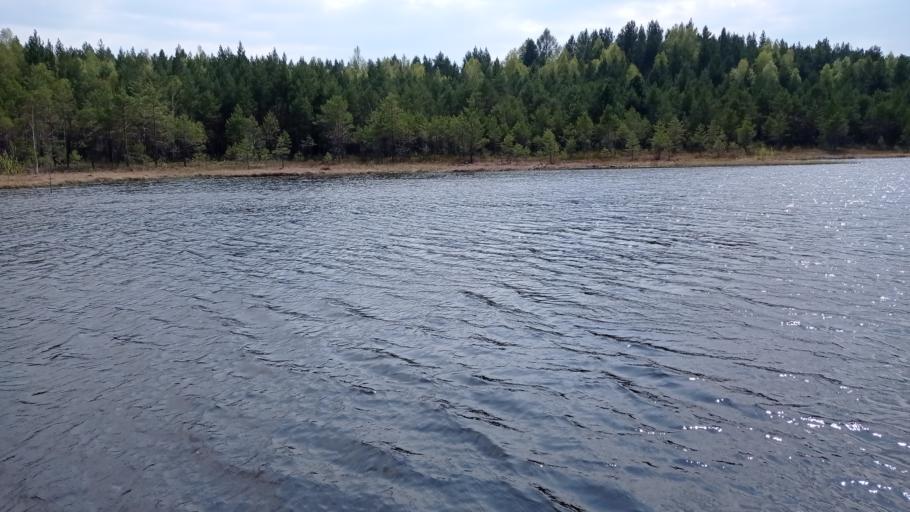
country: RU
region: Tomsk
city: Timiryazevskoye
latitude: 56.4351
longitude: 84.6417
